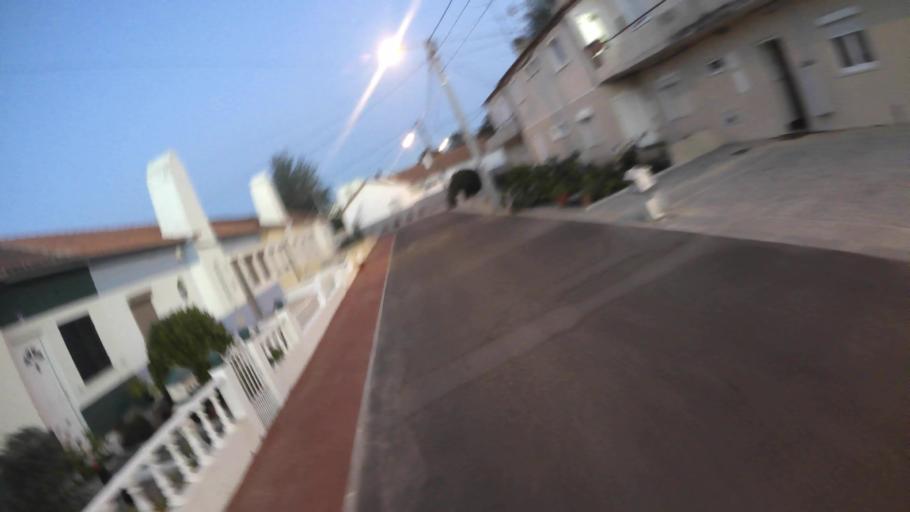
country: PT
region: Aveiro
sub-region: Aveiro
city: Aveiro
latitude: 40.6356
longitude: -8.6572
